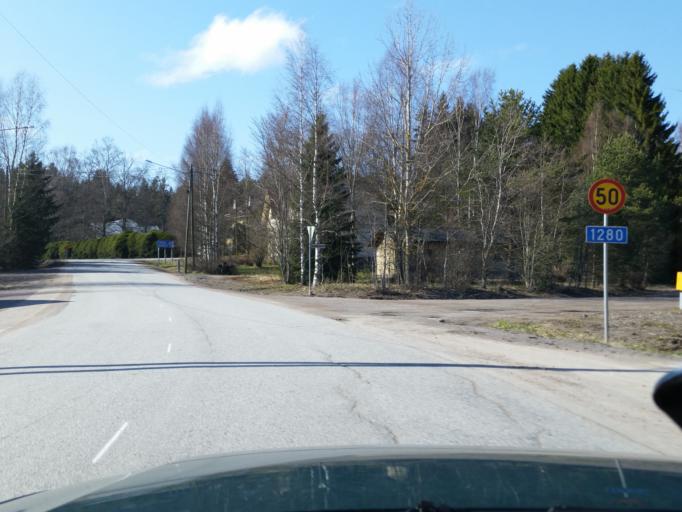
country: FI
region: Uusimaa
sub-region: Helsinki
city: Kaerkoelae
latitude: 60.5084
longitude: 23.9655
